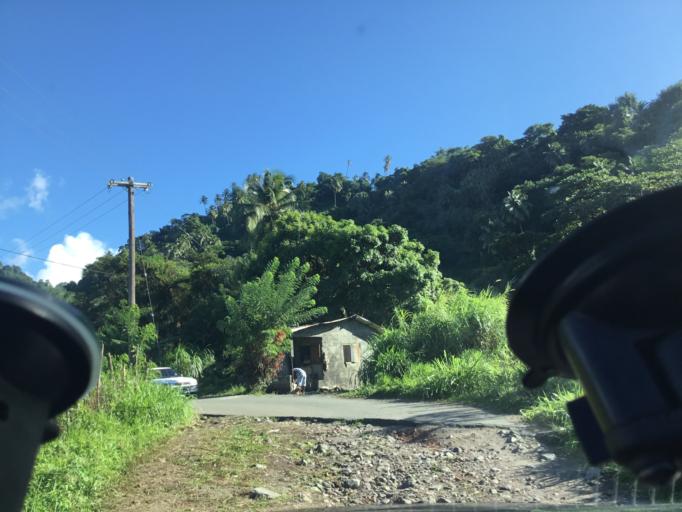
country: VC
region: Saint David
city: Chateaubelair
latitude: 13.3083
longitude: -61.2340
